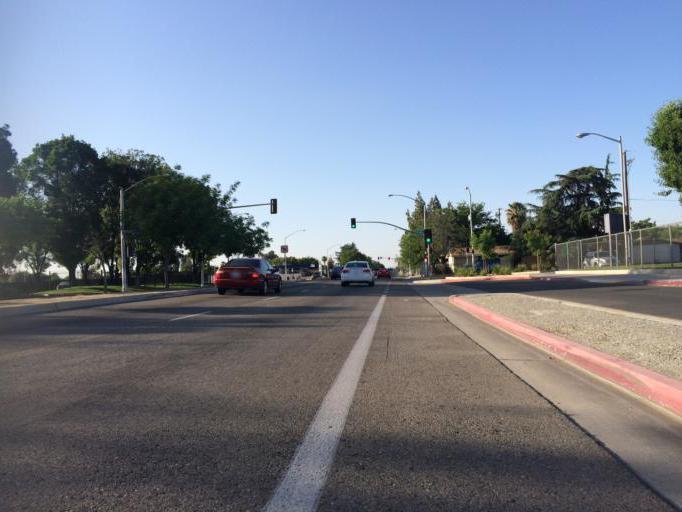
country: US
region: California
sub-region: Fresno County
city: Sunnyside
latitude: 36.7554
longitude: -119.7182
